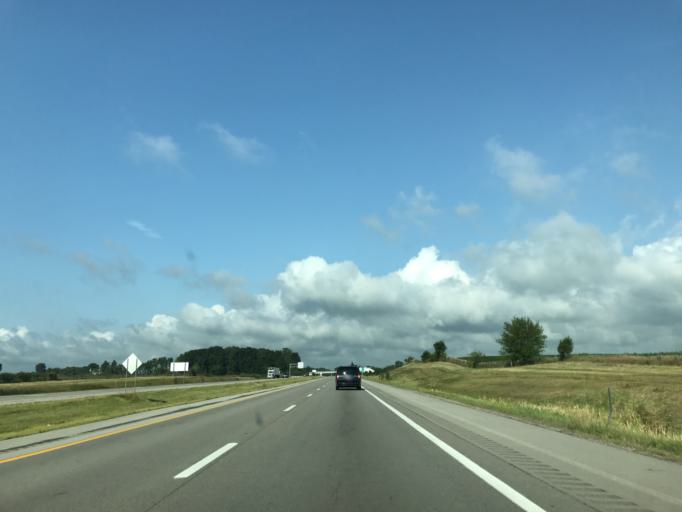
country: US
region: Indiana
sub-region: Steuben County
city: Hamilton
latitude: 41.6305
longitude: -84.7777
